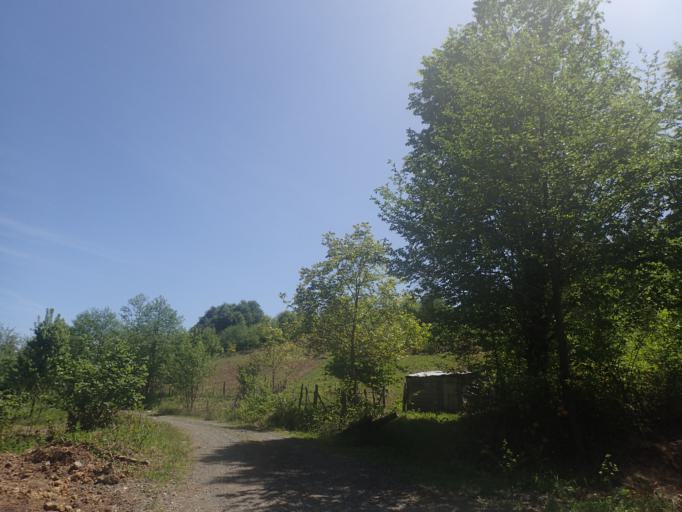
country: TR
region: Ordu
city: Akkus
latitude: 40.8756
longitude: 37.0736
